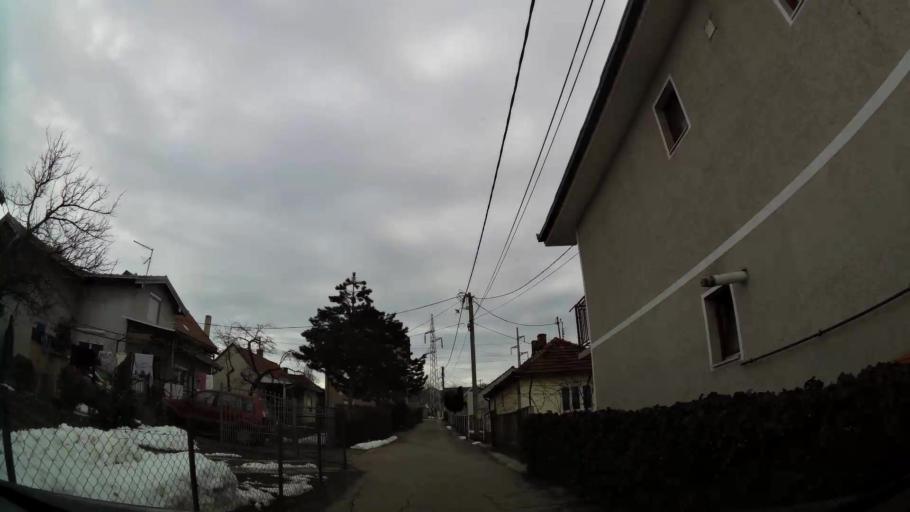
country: RS
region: Central Serbia
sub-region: Belgrade
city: Rakovica
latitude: 44.7444
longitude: 20.3988
